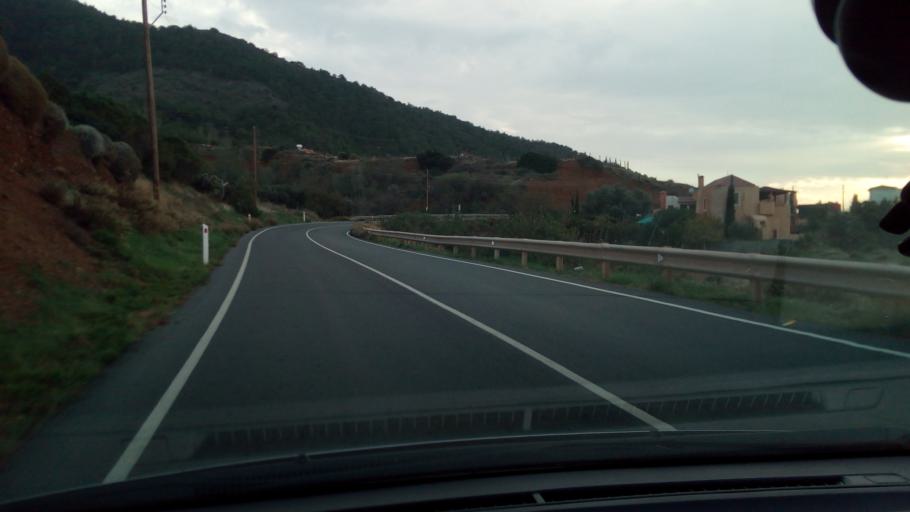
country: CY
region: Lefkosia
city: Kato Pyrgos
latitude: 35.1533
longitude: 32.5408
